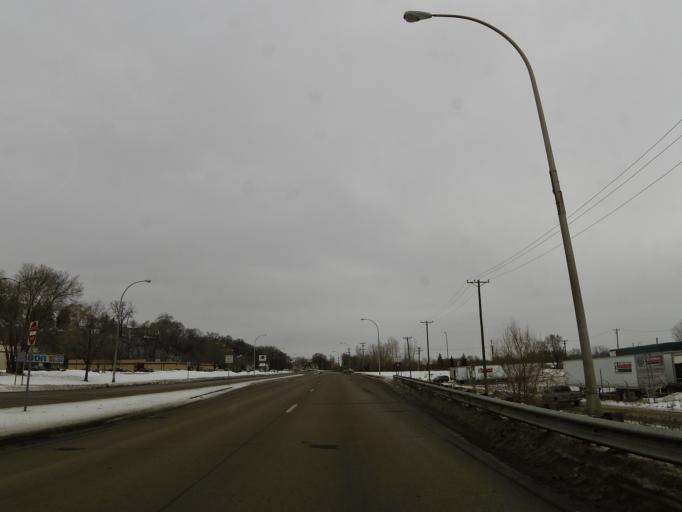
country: US
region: Minnesota
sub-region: Dakota County
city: South Saint Paul
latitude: 44.8953
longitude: -93.0357
